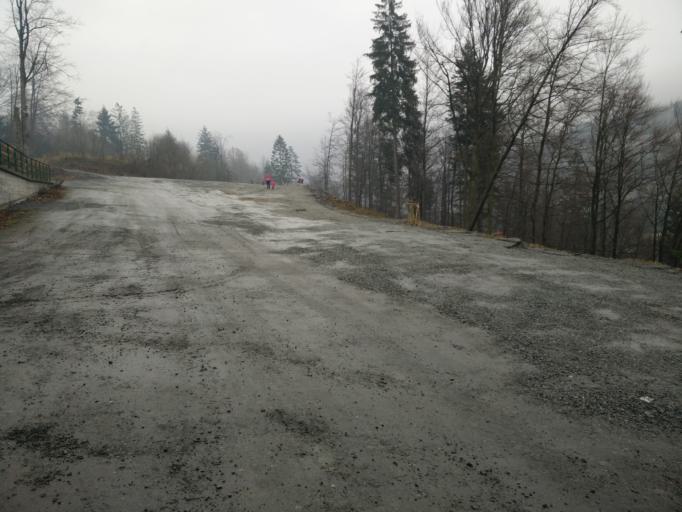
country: PL
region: Silesian Voivodeship
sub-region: Powiat cieszynski
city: Wisla
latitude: 49.6362
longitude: 18.8906
